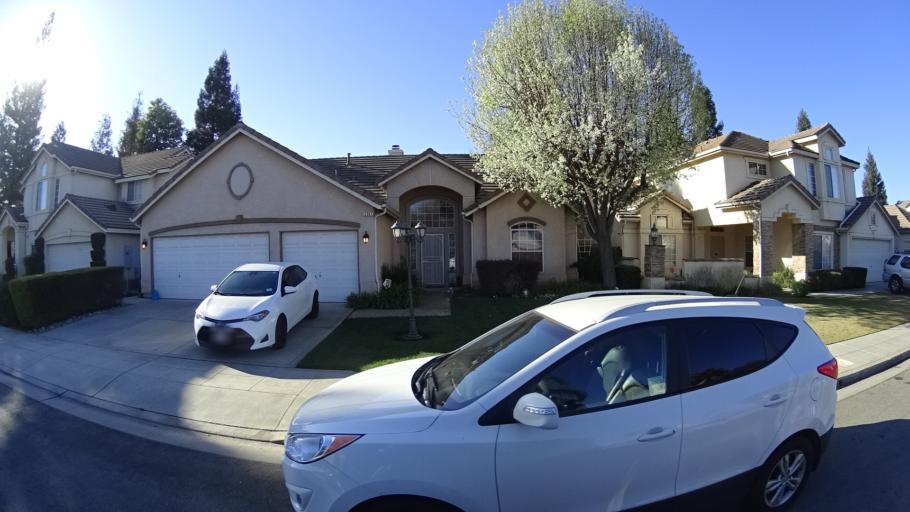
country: US
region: California
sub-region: Fresno County
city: Clovis
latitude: 36.8406
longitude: -119.7405
